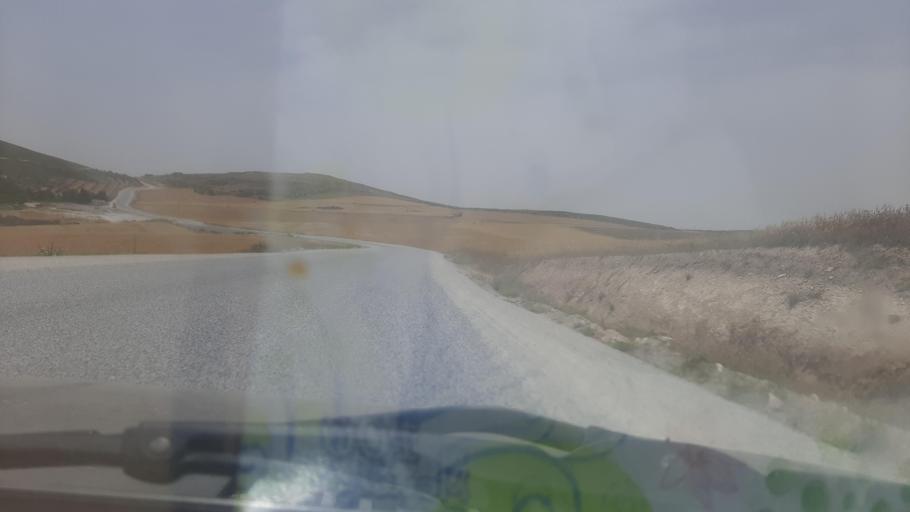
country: TN
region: Tunis
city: La Mohammedia
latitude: 36.5411
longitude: 10.1520
